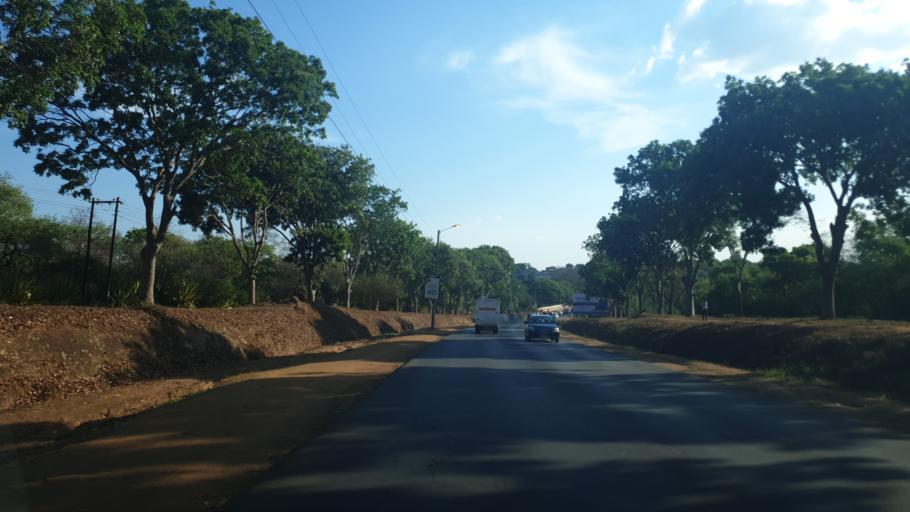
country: MW
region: Central Region
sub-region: Lilongwe District
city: Lilongwe
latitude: -13.9683
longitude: 33.7849
